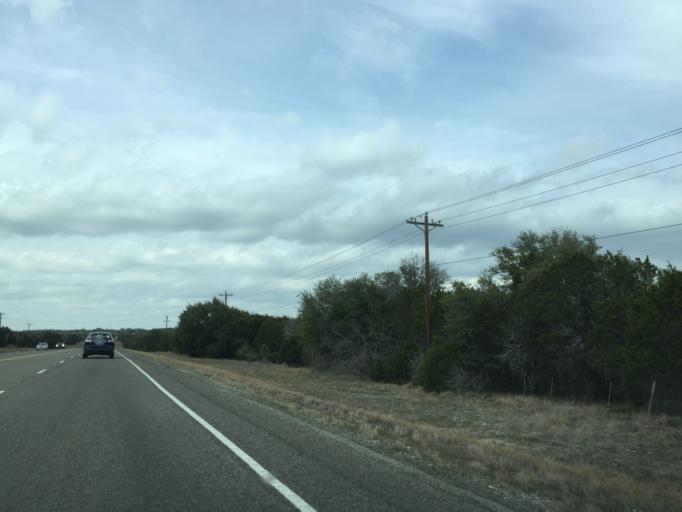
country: US
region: Texas
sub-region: Burnet County
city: Meadowlakes
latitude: 30.4953
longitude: -98.2540
